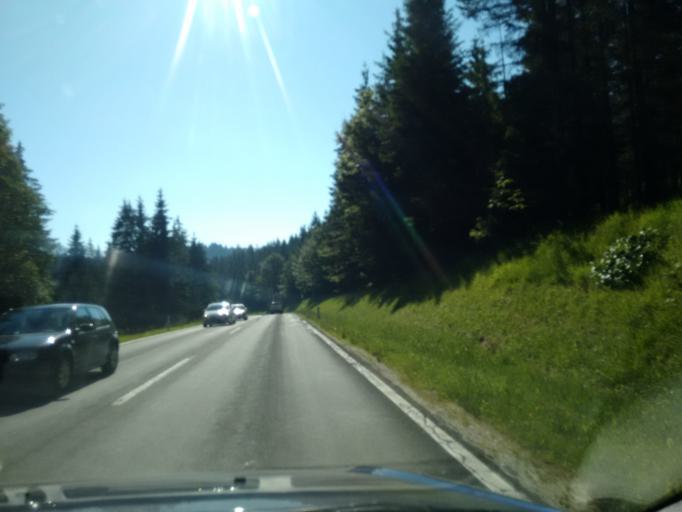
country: AT
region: Styria
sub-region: Politischer Bezirk Liezen
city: Altaussee
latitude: 47.6218
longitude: 13.6976
